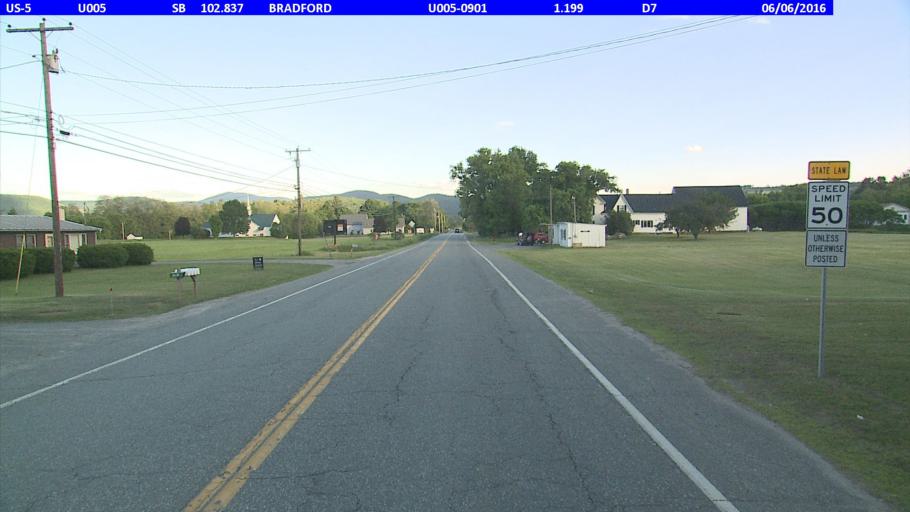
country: US
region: New Hampshire
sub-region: Grafton County
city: Orford
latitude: 43.9787
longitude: -72.1195
